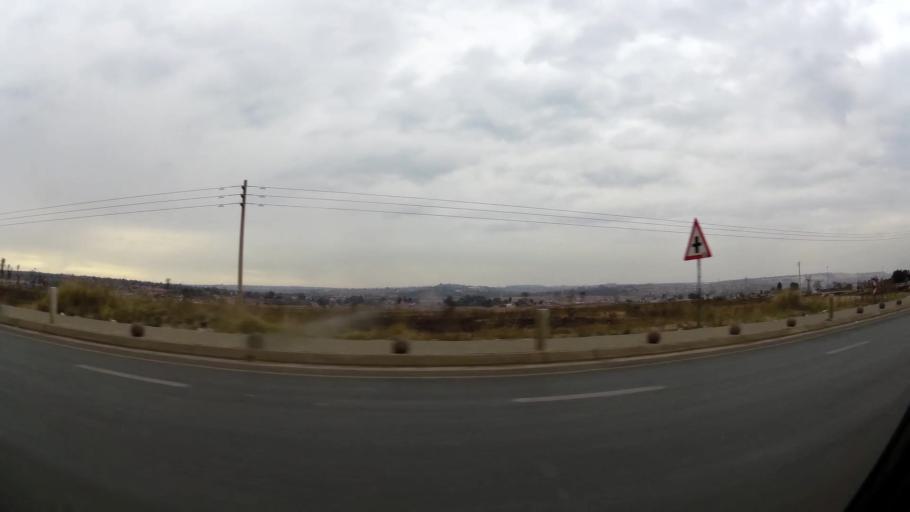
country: ZA
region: Gauteng
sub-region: City of Johannesburg Metropolitan Municipality
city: Roodepoort
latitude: -26.1742
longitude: 27.8088
